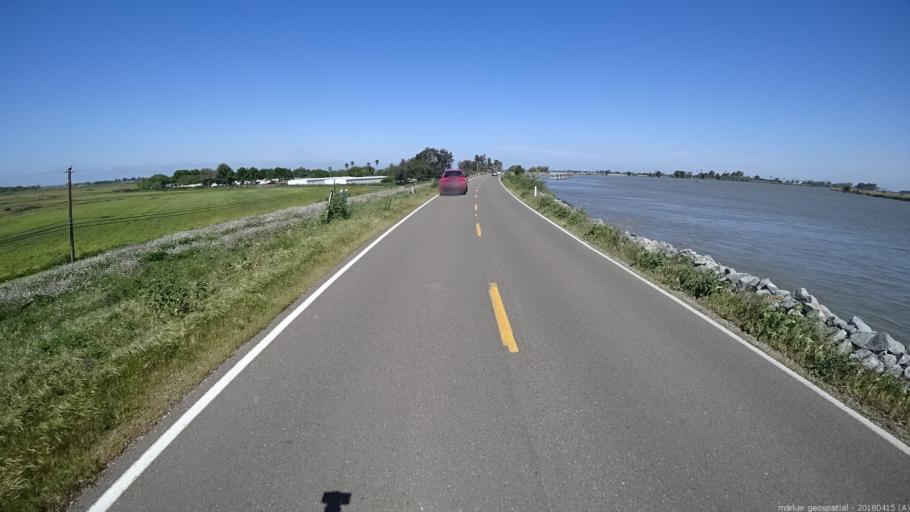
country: US
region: California
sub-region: Contra Costa County
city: Bethel Island
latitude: 38.1119
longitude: -121.5845
